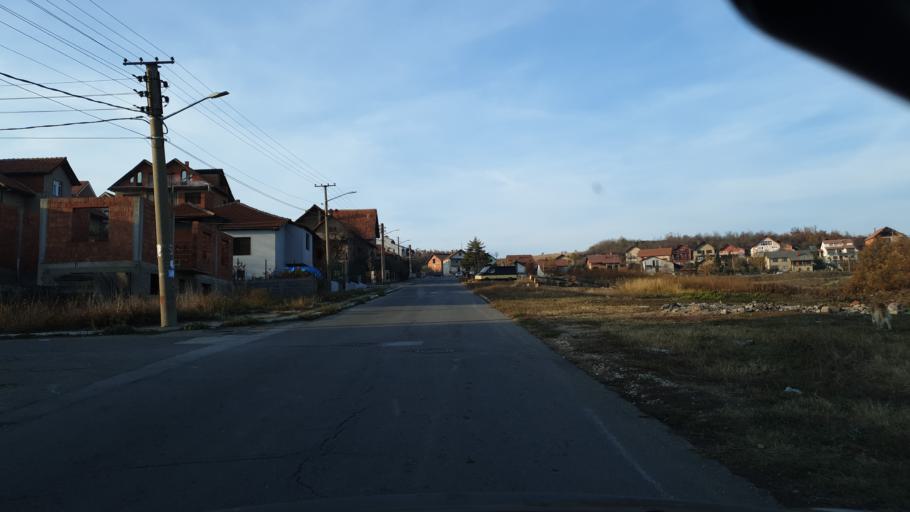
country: RS
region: Central Serbia
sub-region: Borski Okrug
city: Bor
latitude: 44.0555
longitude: 22.0867
